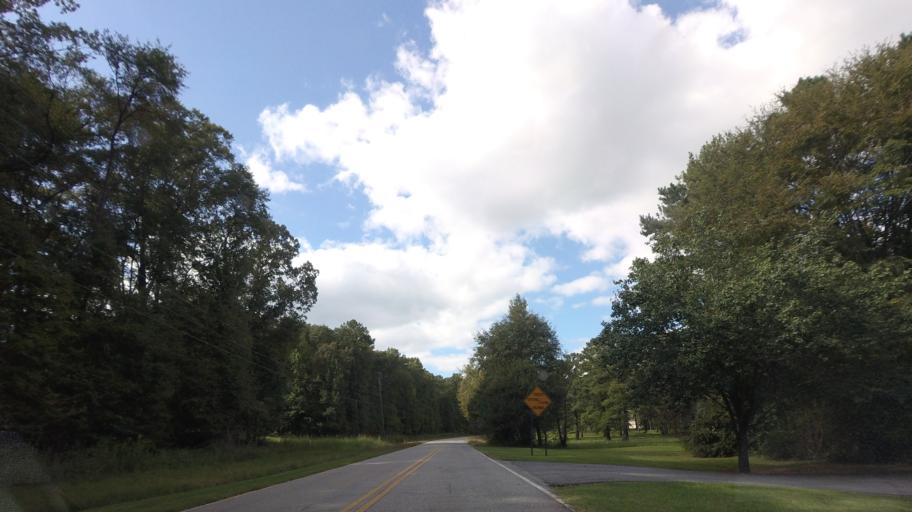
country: US
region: Georgia
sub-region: Bibb County
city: Macon
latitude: 32.9259
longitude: -83.7019
